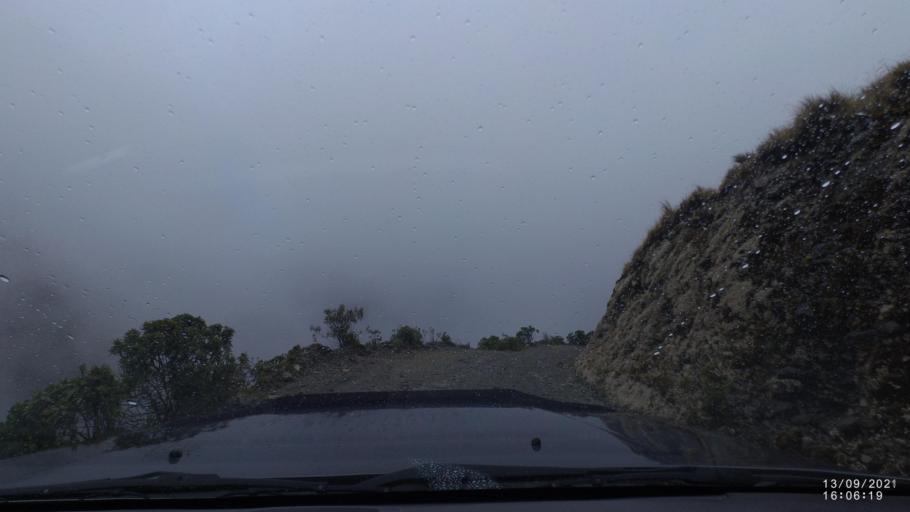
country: BO
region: Cochabamba
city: Colomi
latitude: -17.2826
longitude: -65.7105
